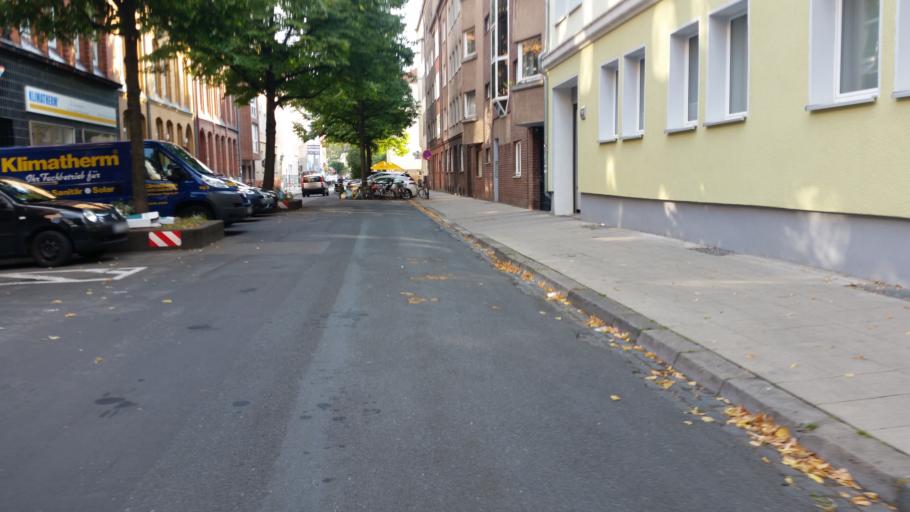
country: DE
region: Lower Saxony
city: Hannover
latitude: 52.3836
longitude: 9.7496
